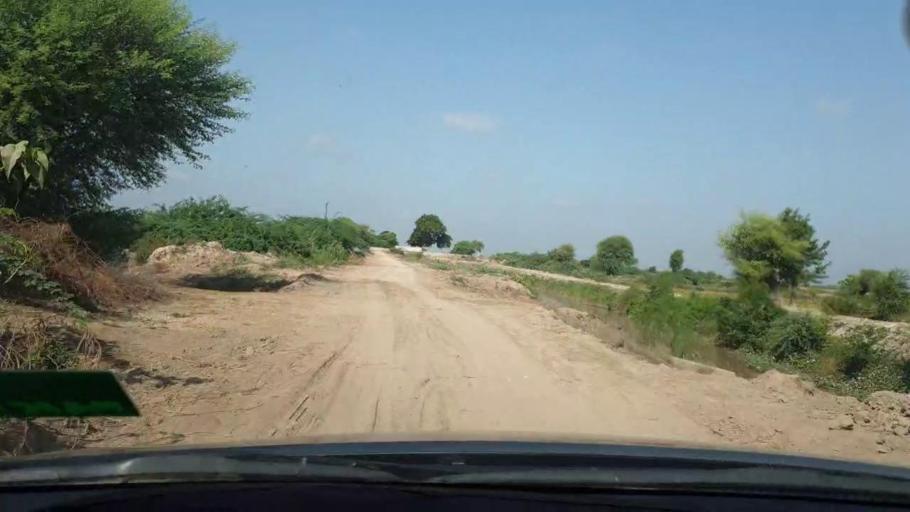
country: PK
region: Sindh
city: Tando Bago
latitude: 24.8756
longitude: 69.0019
